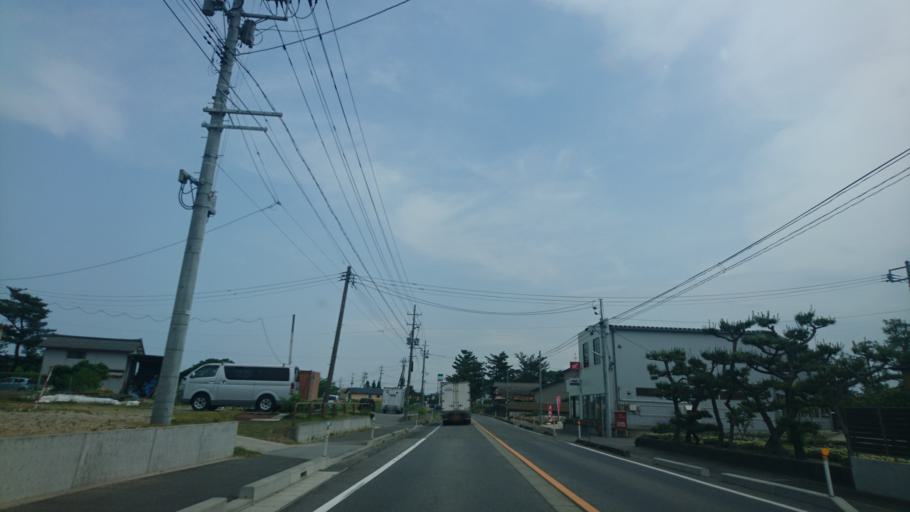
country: JP
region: Niigata
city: Shibata
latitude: 38.0062
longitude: 139.2699
